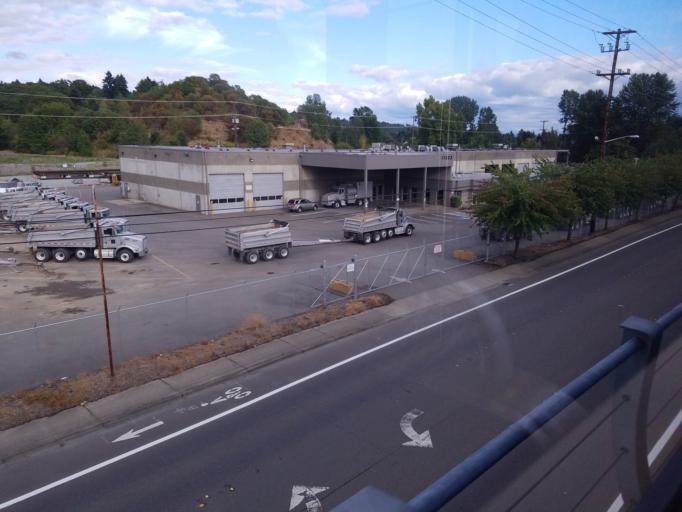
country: US
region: Washington
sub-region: King County
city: Riverton
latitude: 47.5025
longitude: -122.2888
